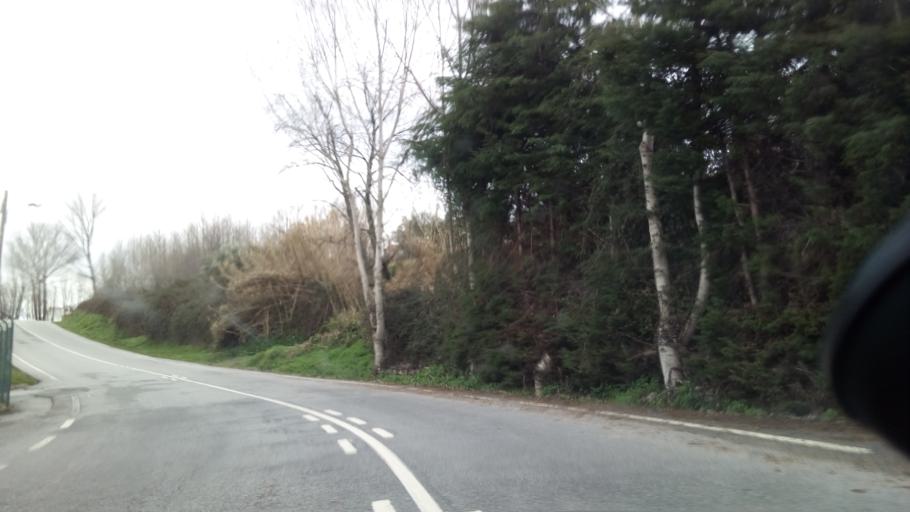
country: PT
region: Guarda
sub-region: Manteigas
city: Manteigas
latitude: 40.4959
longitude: -7.5982
